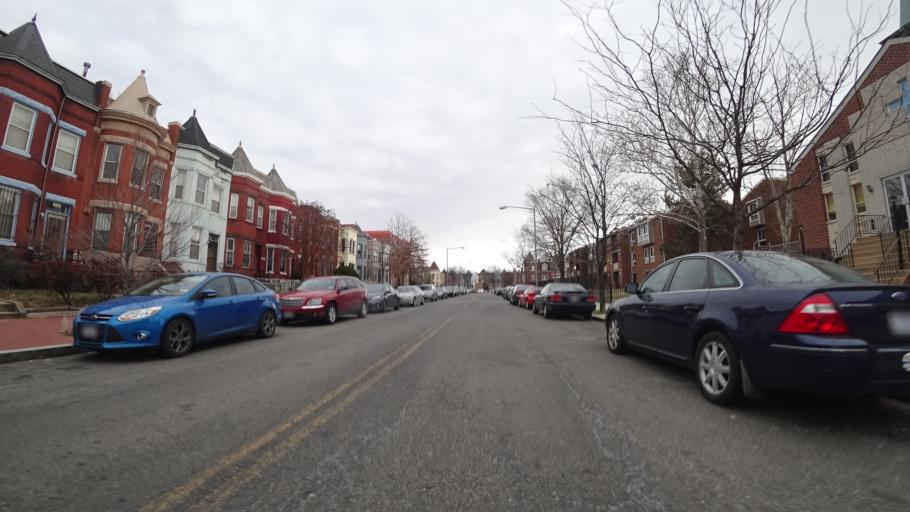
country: US
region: Washington, D.C.
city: Washington, D.C.
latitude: 38.9115
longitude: -77.0152
